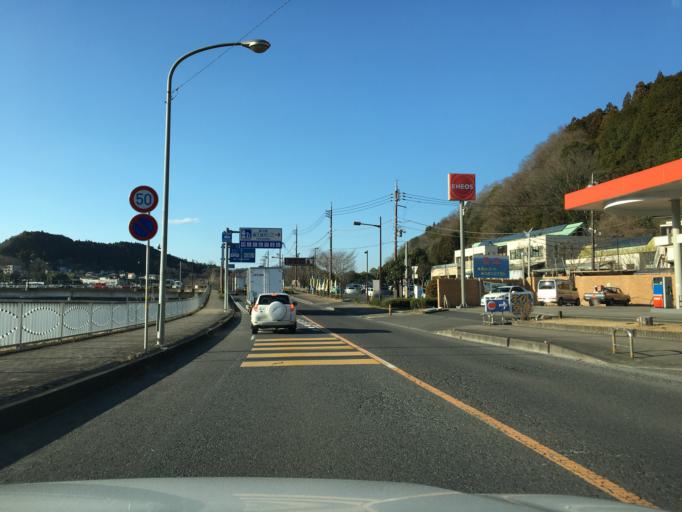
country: JP
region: Ibaraki
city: Daigo
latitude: 36.7672
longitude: 140.3590
